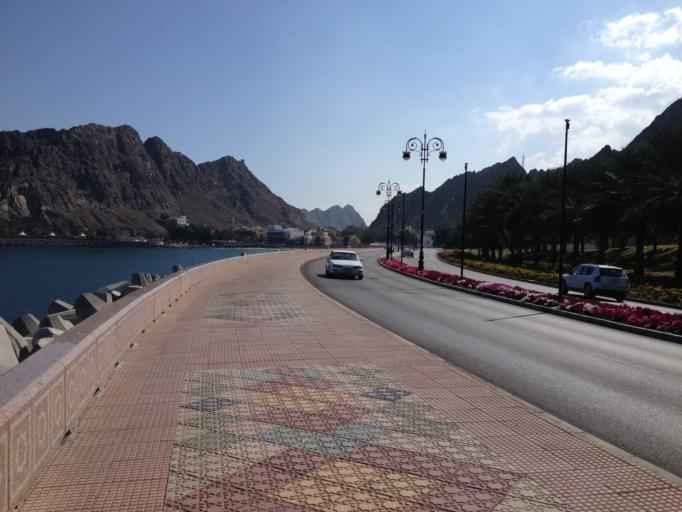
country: OM
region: Muhafazat Masqat
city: Muscat
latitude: 23.6242
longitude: 58.5805
